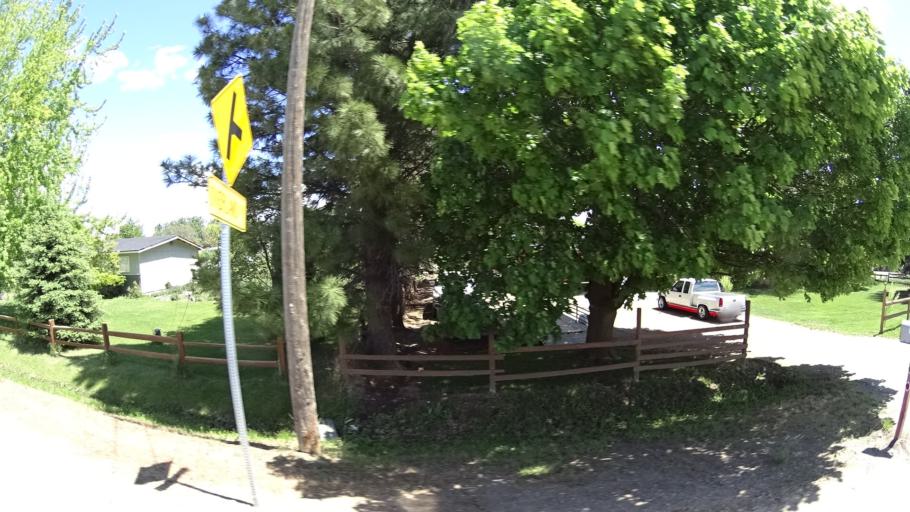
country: US
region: Idaho
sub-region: Ada County
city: Meridian
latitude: 43.5890
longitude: -116.4735
